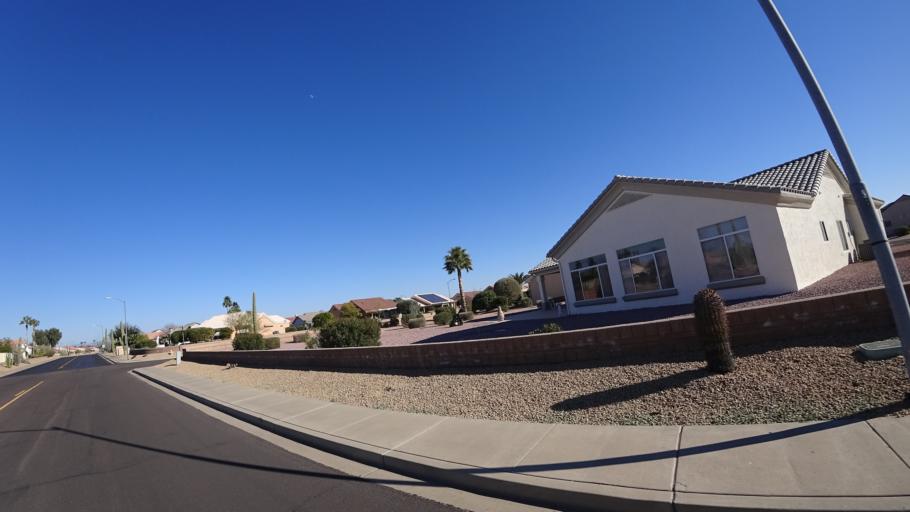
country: US
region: Arizona
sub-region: Maricopa County
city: Sun City West
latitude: 33.6925
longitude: -112.3784
